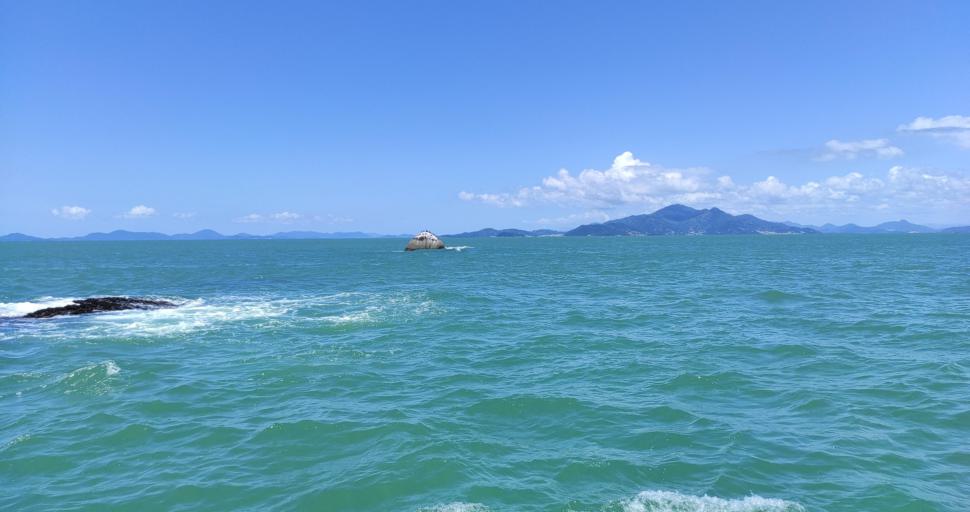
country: BR
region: Santa Catarina
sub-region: Porto Belo
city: Porto Belo
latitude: -27.2225
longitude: -48.5127
